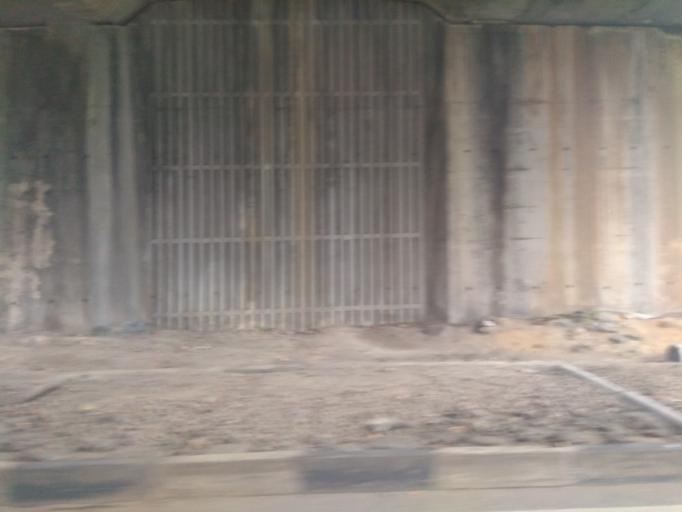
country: MY
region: Johor
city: Johor Bahru
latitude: 1.4889
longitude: 103.7403
